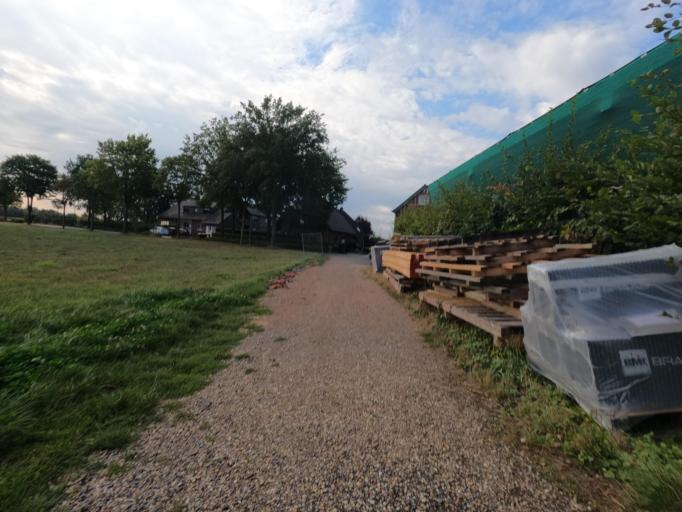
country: DE
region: North Rhine-Westphalia
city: Wegberg
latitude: 51.1090
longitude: 6.2635
